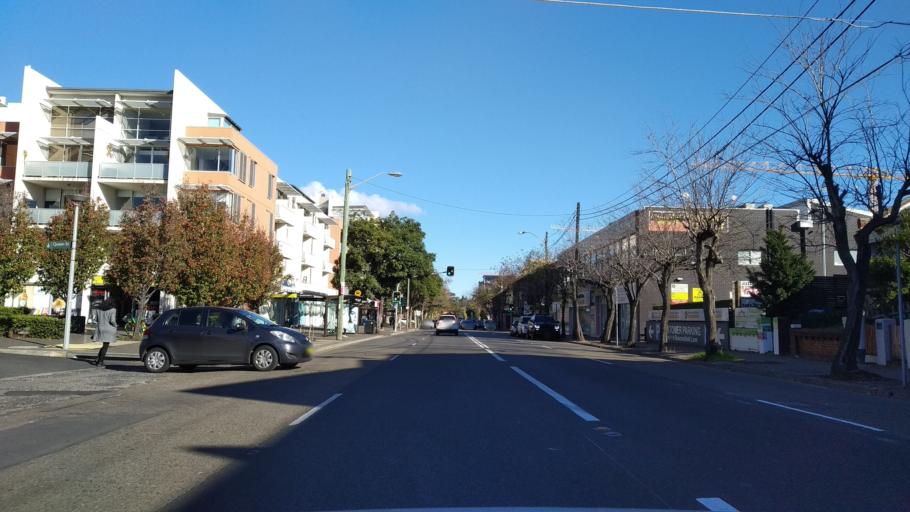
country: AU
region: New South Wales
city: Alexandria
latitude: -33.9139
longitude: 151.2011
